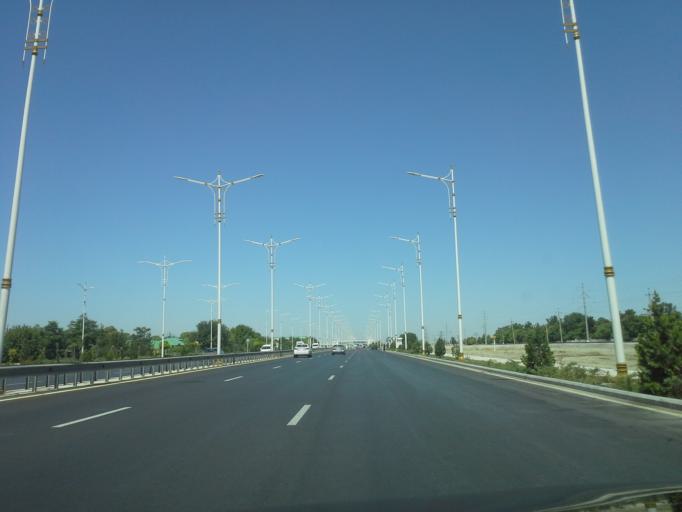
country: TM
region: Ahal
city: Ashgabat
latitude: 37.9699
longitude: 58.3528
